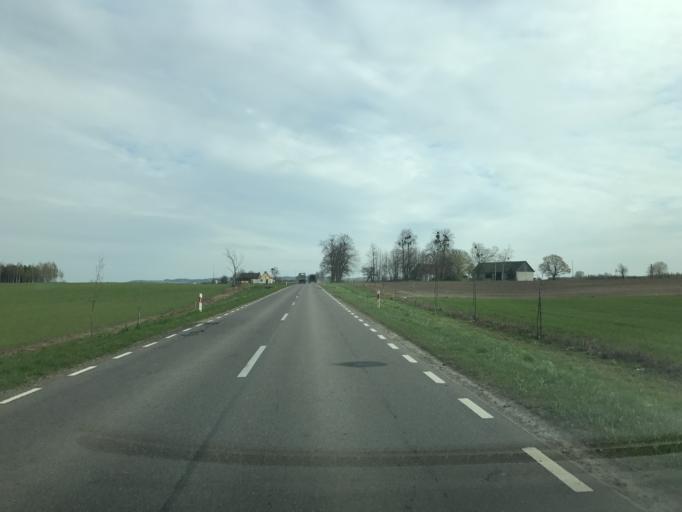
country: PL
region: Warmian-Masurian Voivodeship
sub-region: Powiat ostrodzki
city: Gierzwald
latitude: 53.5109
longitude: 20.0846
